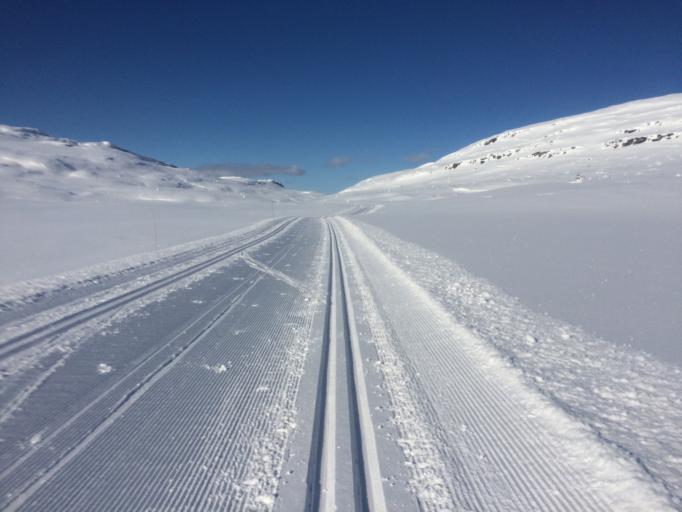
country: NO
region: Oppland
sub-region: Ringebu
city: Ringebu
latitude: 61.3815
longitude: 10.0602
